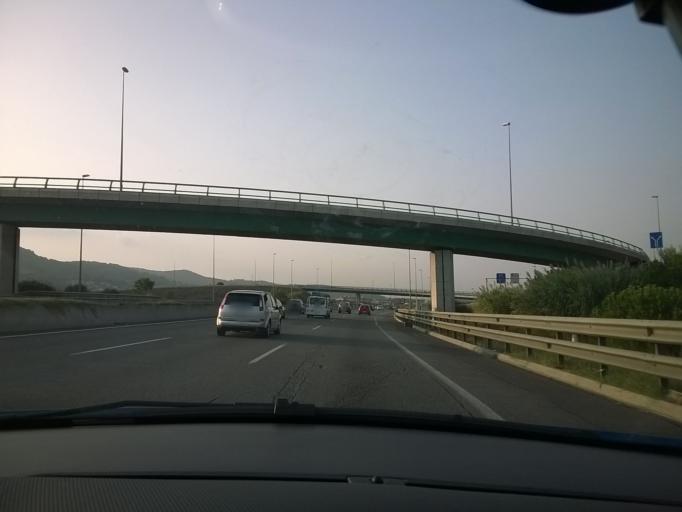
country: ES
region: Catalonia
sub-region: Provincia de Barcelona
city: Molins de Rei
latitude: 41.4150
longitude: 2.0055
